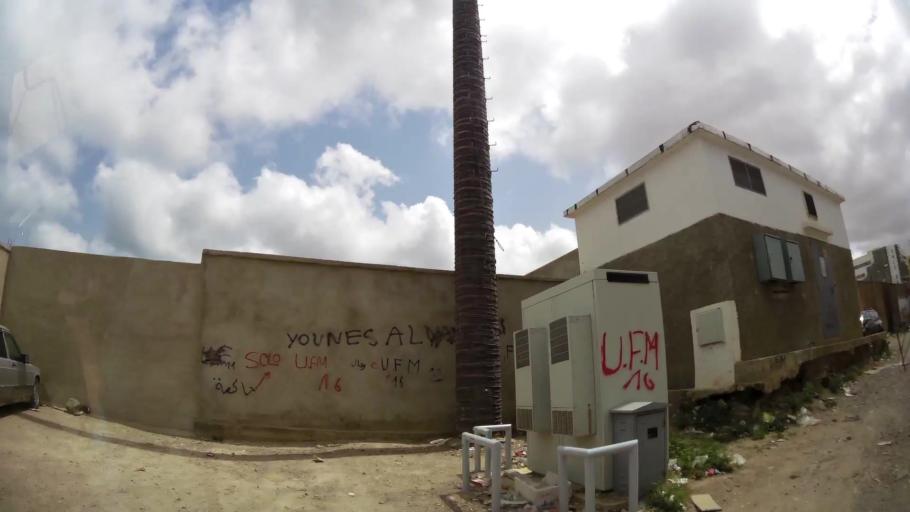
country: MA
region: Oriental
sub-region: Nador
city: Nador
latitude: 35.1771
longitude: -2.9221
